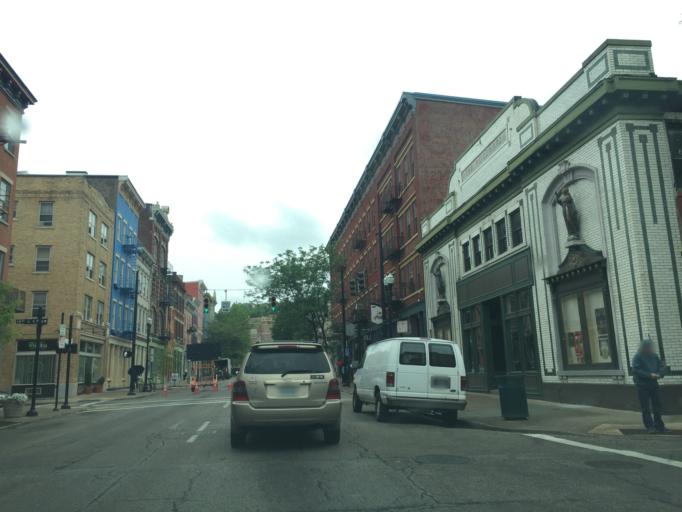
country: US
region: Kentucky
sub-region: Campbell County
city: Newport
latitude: 39.1111
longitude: -84.5121
